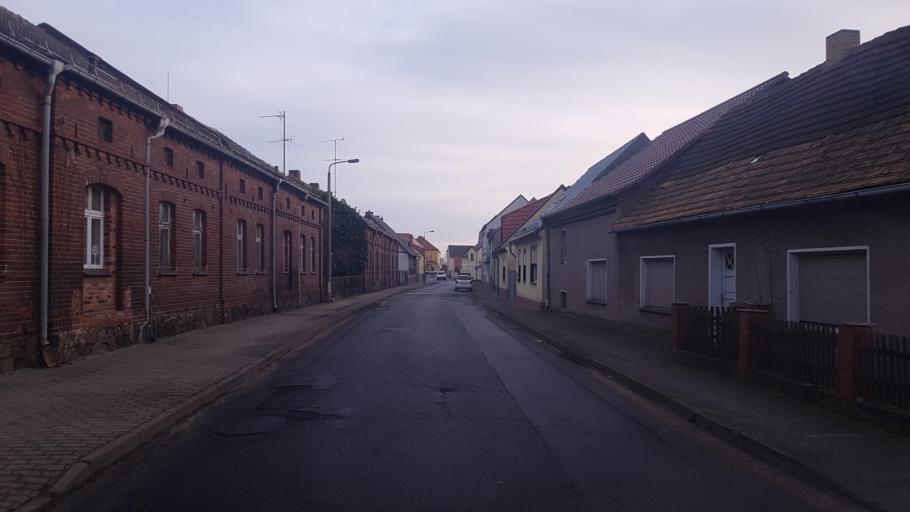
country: DE
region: Brandenburg
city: Golssen
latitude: 51.9695
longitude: 13.6016
